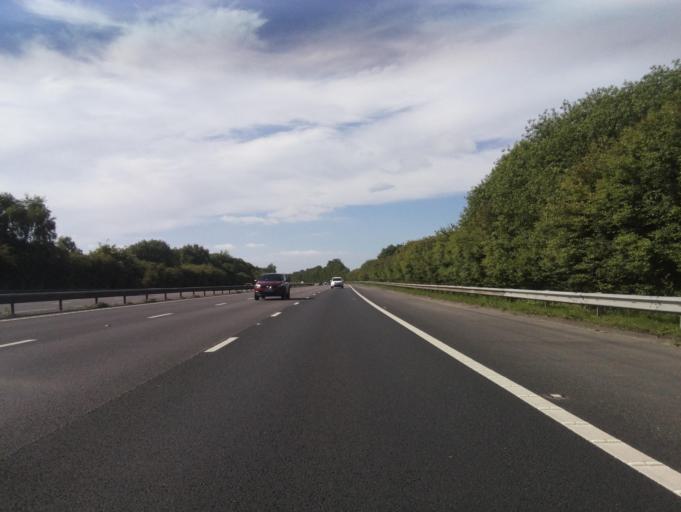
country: GB
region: England
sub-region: Borough of Bolton
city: Horwich
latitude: 53.5852
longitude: -2.5555
